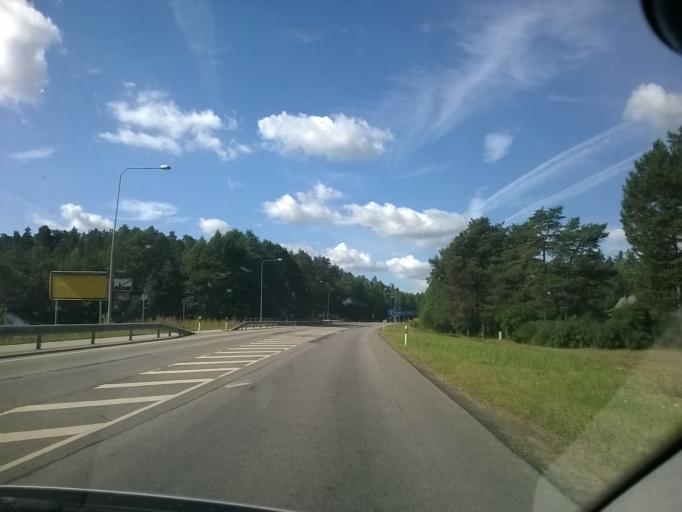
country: EE
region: Vorumaa
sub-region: Voru linn
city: Voru
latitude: 57.8193
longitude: 26.9979
